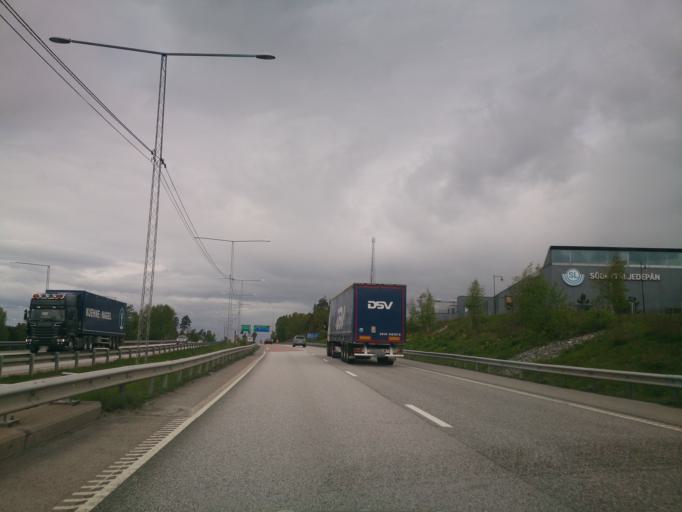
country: SE
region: Stockholm
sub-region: Sodertalje Kommun
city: Pershagen
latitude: 59.1742
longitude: 17.6460
